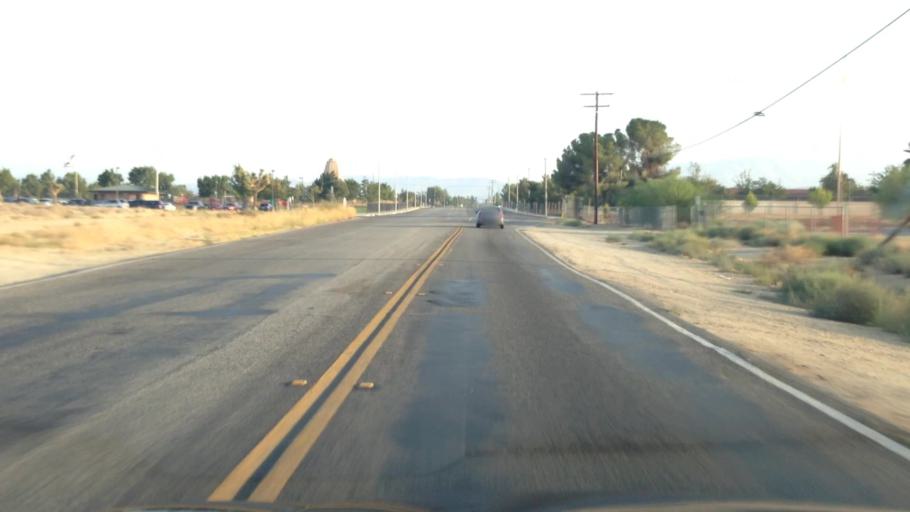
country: US
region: California
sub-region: Los Angeles County
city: Quartz Hill
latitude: 34.6504
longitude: -118.1832
